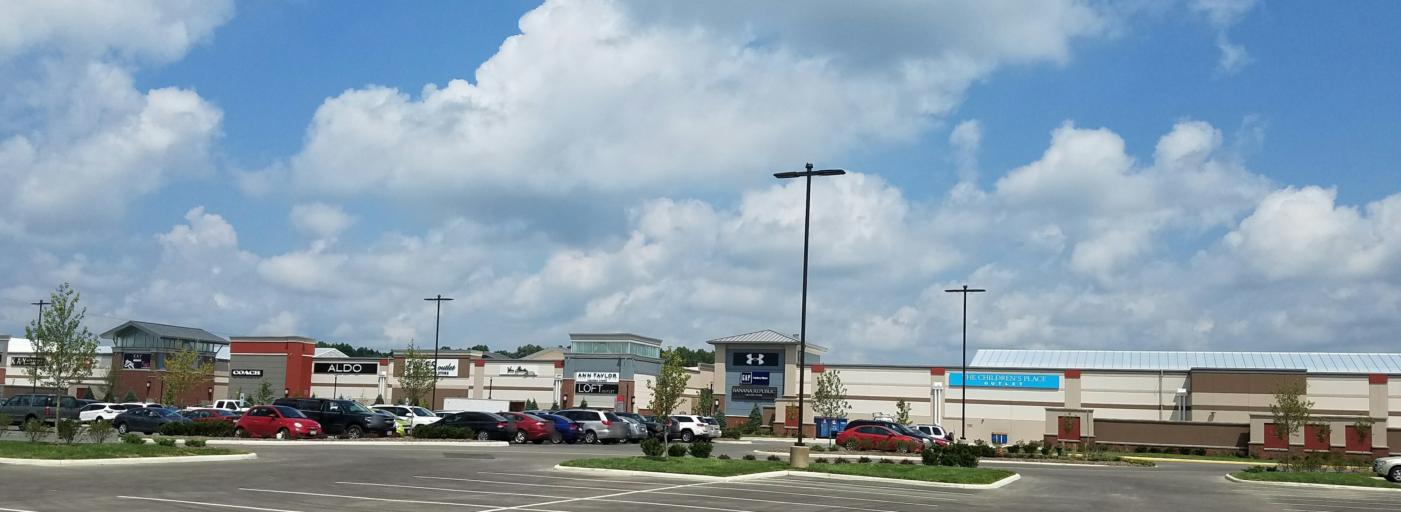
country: US
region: Ohio
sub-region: Delaware County
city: Sunbury
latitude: 40.2583
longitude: -82.9255
